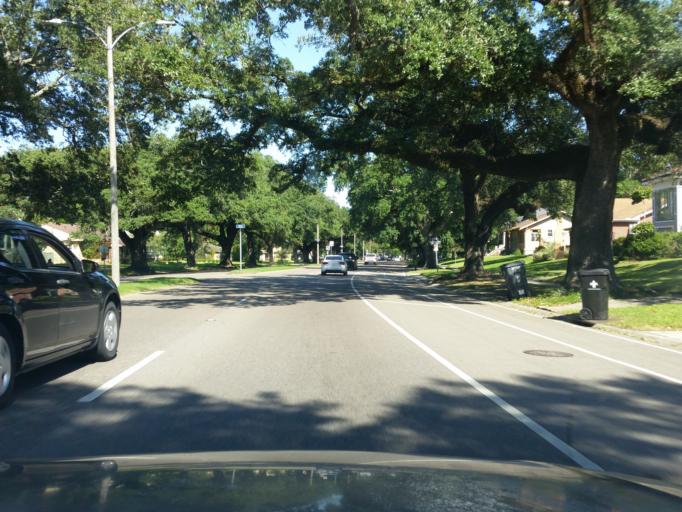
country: US
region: Louisiana
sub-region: Orleans Parish
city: New Orleans
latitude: 30.0028
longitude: -90.0535
